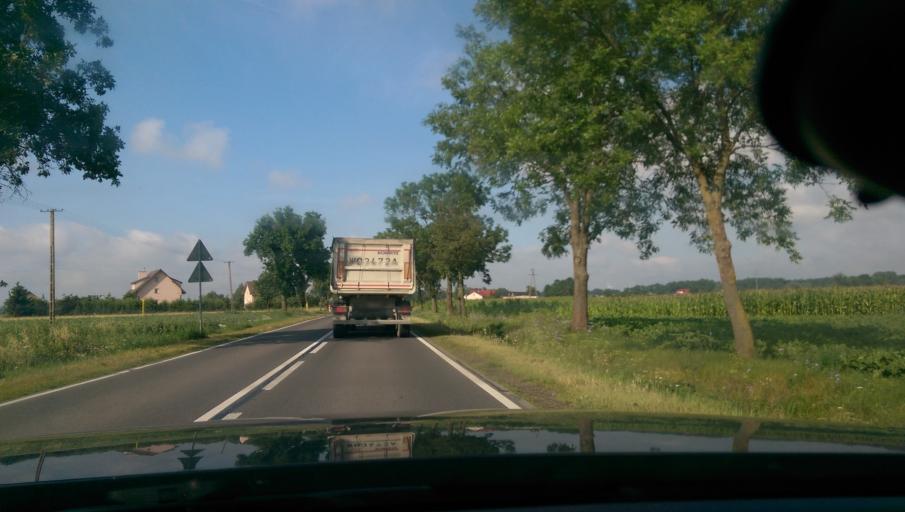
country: PL
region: Masovian Voivodeship
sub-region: Powiat ciechanowski
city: Opinogora Gorna
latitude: 52.9241
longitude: 20.6694
